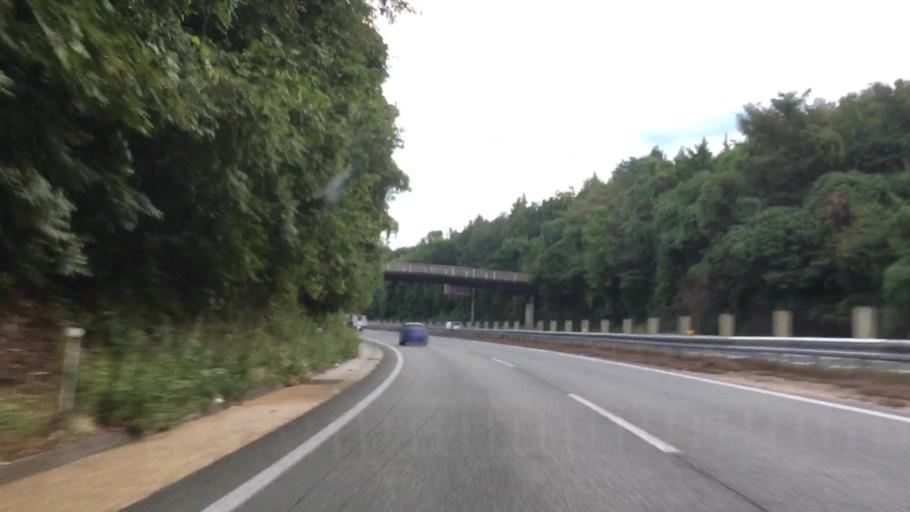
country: JP
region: Yamaguchi
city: Ogori-shimogo
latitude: 34.1678
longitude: 131.2412
